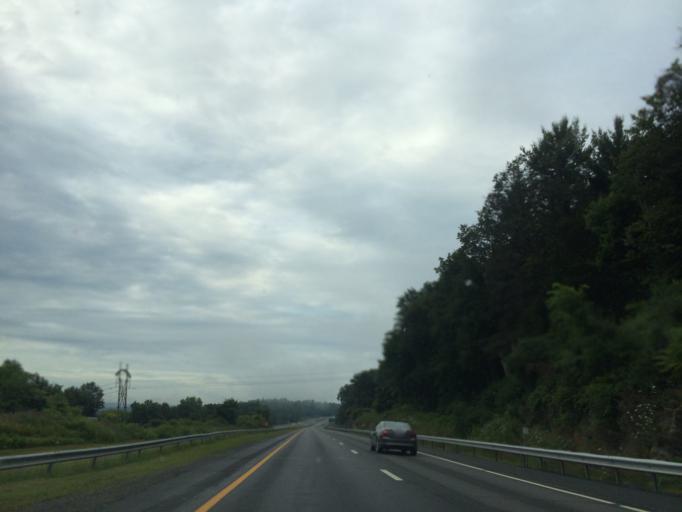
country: US
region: New York
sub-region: Greene County
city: Jefferson Heights
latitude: 42.2641
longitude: -73.8769
